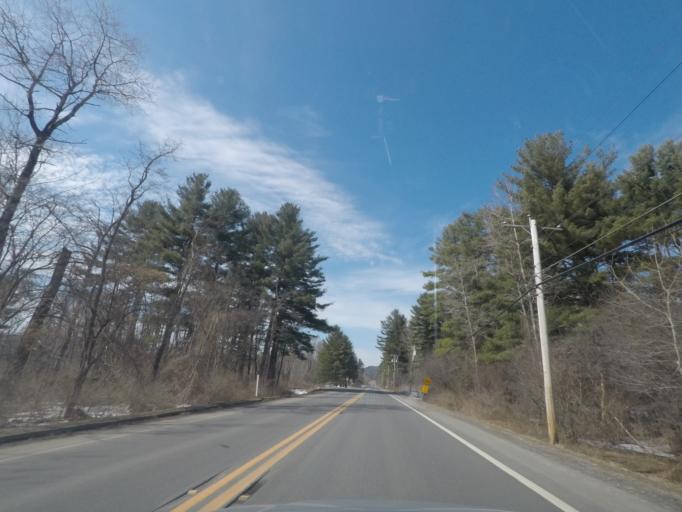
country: US
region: Massachusetts
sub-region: Berkshire County
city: Stockbridge
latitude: 42.2930
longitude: -73.3224
